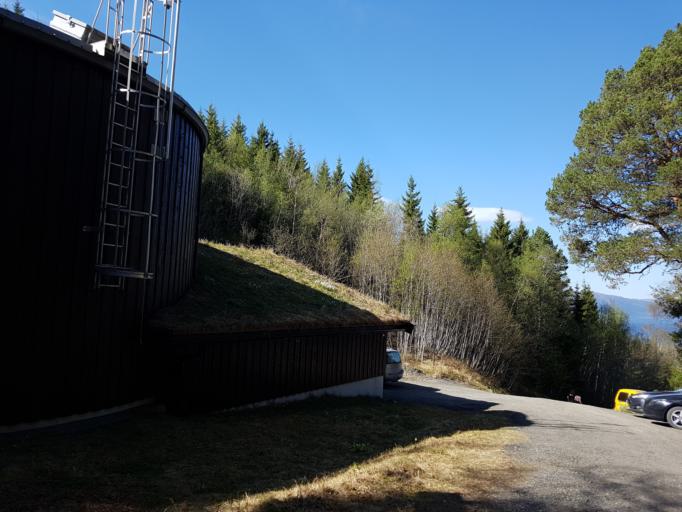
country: NO
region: Sor-Trondelag
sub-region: Trondheim
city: Trondheim
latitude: 63.4478
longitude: 10.3018
